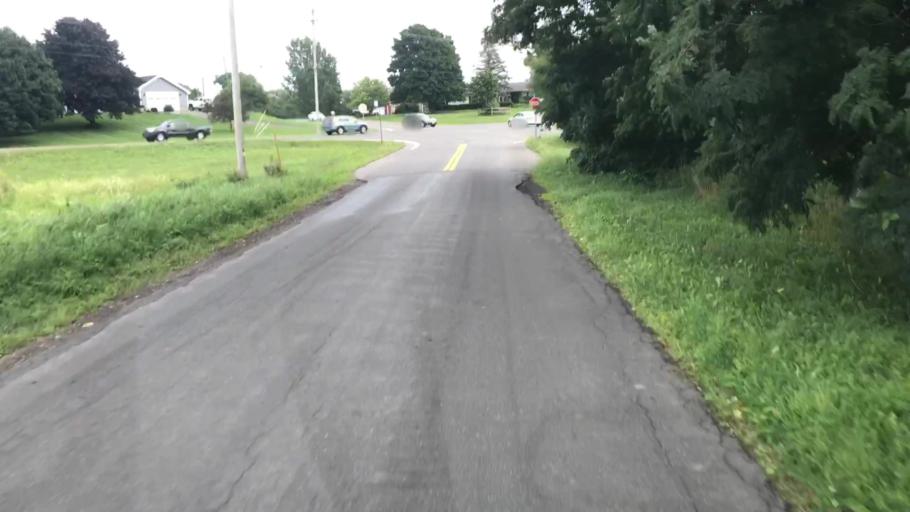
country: US
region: New York
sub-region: Onondaga County
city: Elbridge
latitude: 42.9964
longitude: -76.4406
